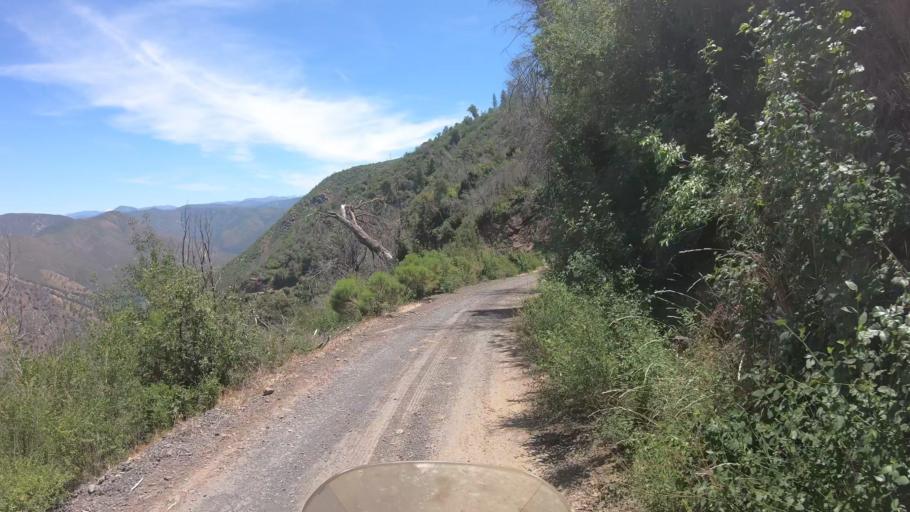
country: US
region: California
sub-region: Tuolumne County
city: Tuolumne City
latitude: 37.8316
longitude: -120.1068
